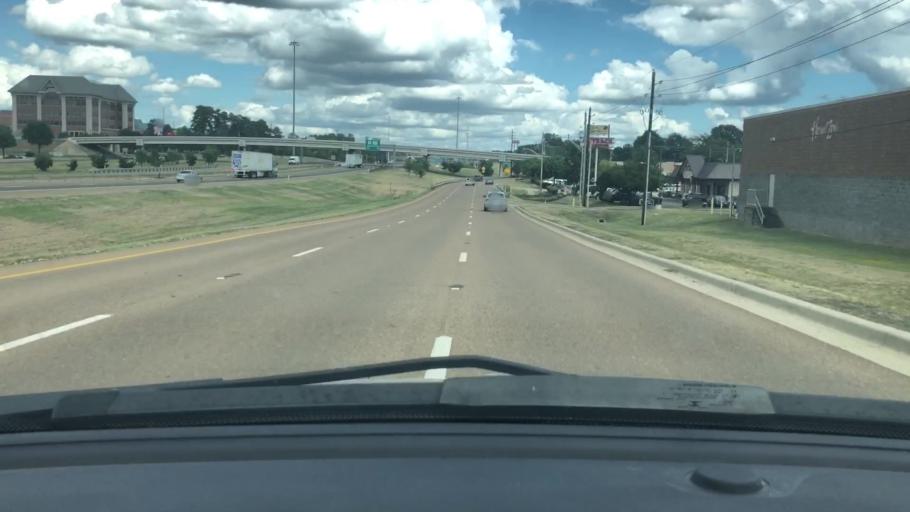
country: US
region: Texas
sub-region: Bowie County
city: Wake Village
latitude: 33.4591
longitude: -94.0798
